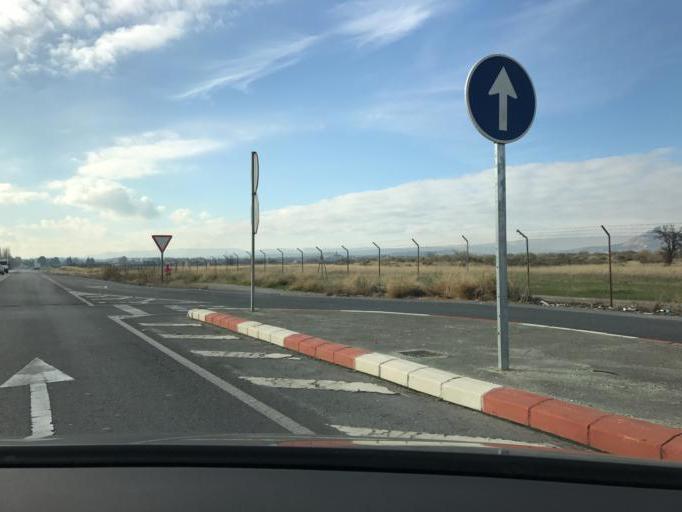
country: ES
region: Andalusia
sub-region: Provincia de Granada
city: Alhendin
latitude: 37.1240
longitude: -3.6312
